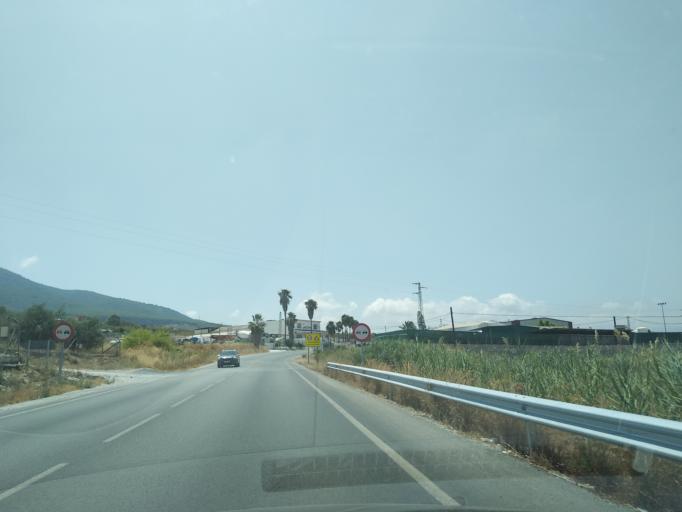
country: ES
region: Andalusia
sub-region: Provincia de Malaga
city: Alhaurin el Grande
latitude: 36.6570
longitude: -4.6750
